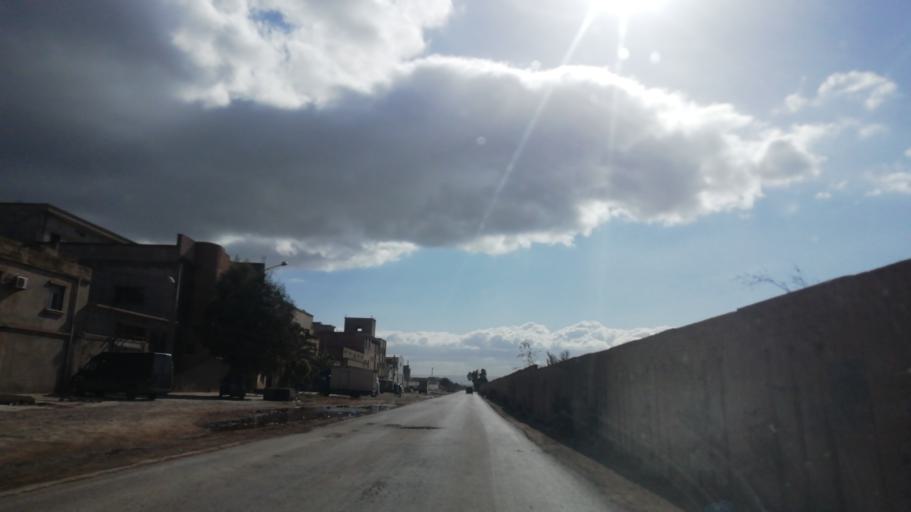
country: DZ
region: Oran
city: Es Senia
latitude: 35.6440
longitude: -0.6031
